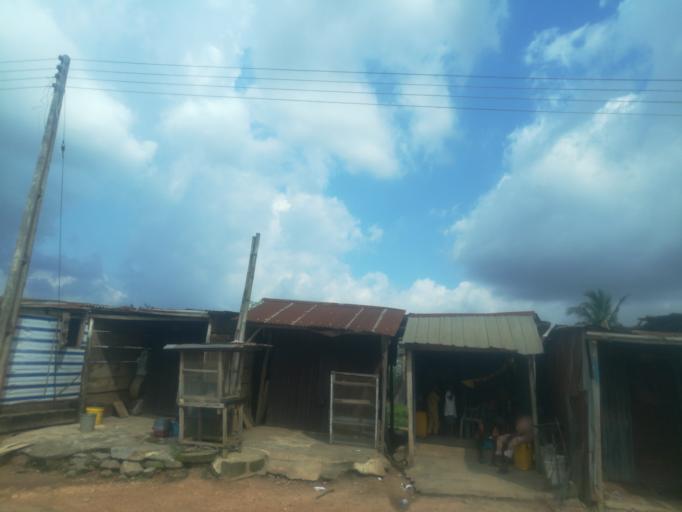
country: NG
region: Oyo
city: Ibadan
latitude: 7.4096
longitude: 3.8244
